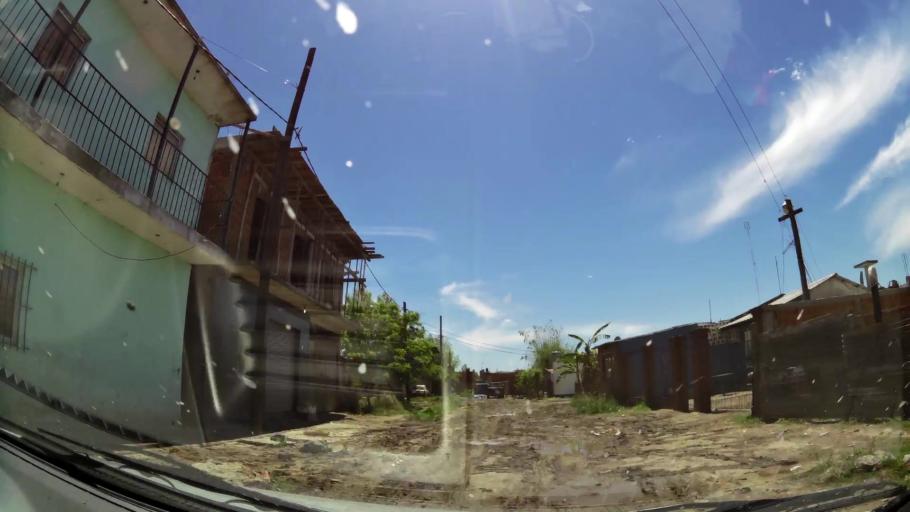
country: AR
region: Buenos Aires
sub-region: Partido de Quilmes
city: Quilmes
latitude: -34.7416
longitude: -58.3112
